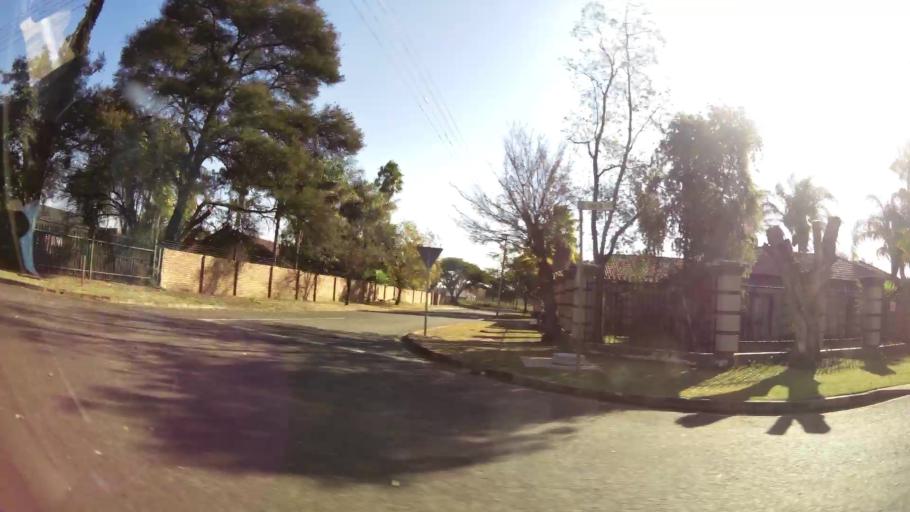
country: ZA
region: Gauteng
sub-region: City of Tshwane Metropolitan Municipality
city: Pretoria
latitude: -25.7267
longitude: 28.2665
